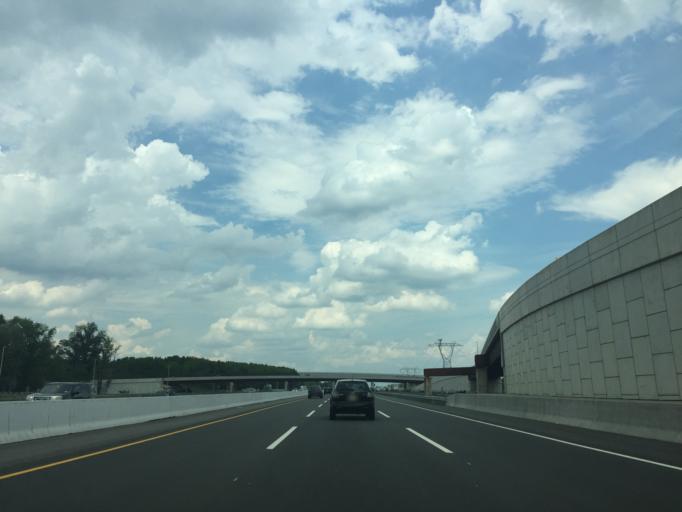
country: US
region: New Jersey
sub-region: Mercer County
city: Yardville
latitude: 40.1695
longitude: -74.6427
